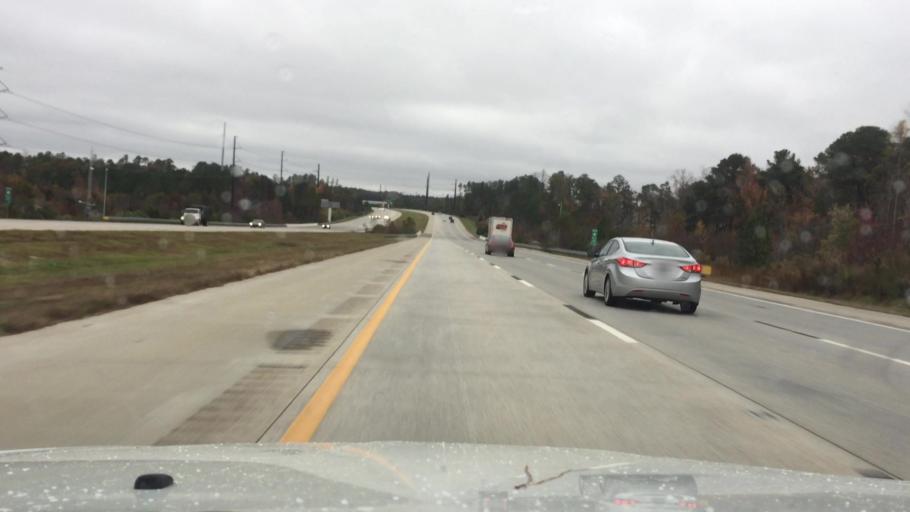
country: US
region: North Carolina
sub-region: Wake County
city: Green Level
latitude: 35.8128
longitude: -78.8921
